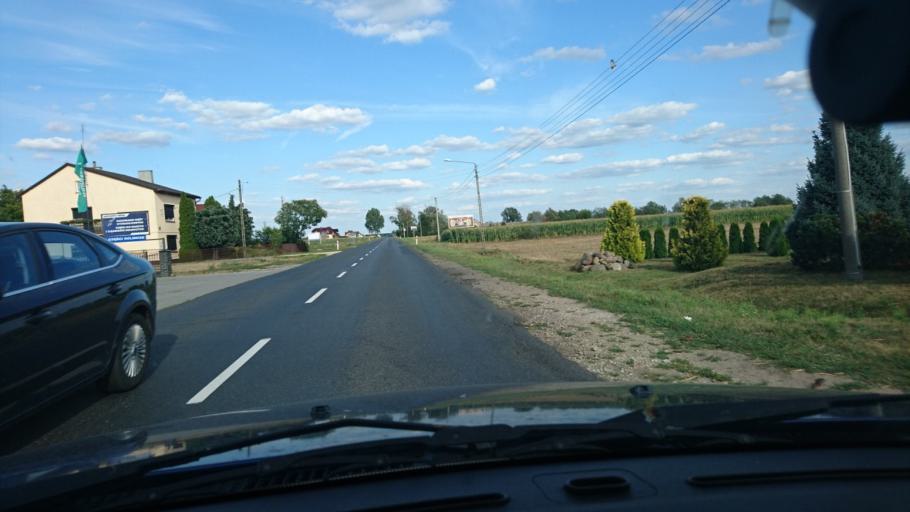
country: PL
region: Greater Poland Voivodeship
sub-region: Powiat krotoszynski
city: Sulmierzyce
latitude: 51.6055
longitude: 17.5425
